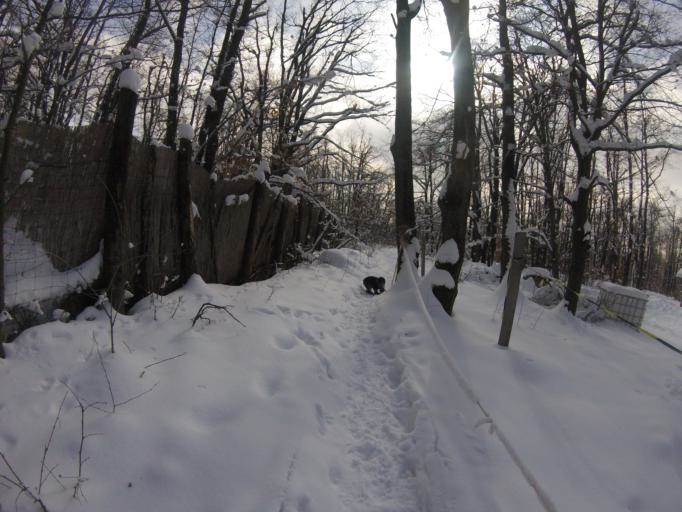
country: HU
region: Pest
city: Pilisszentkereszt
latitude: 47.7137
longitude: 18.8965
